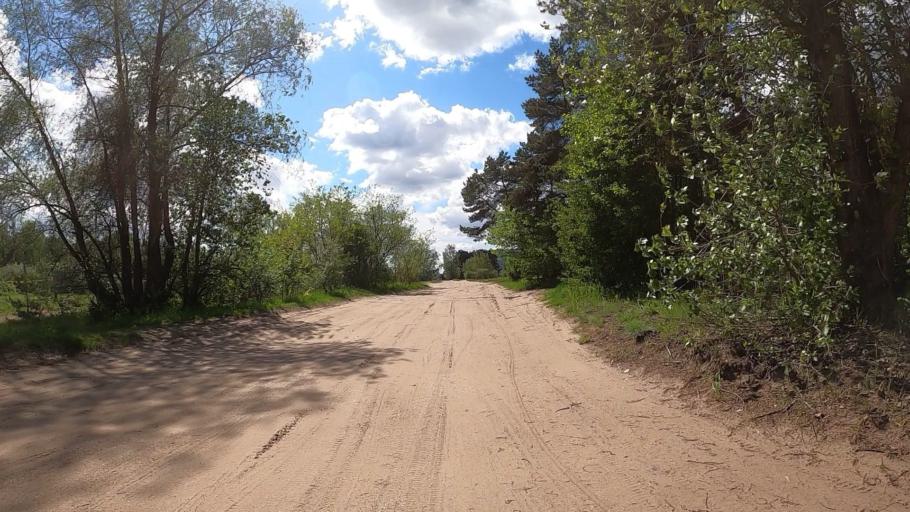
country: LV
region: Kekava
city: Balozi
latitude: 56.9018
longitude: 24.1106
